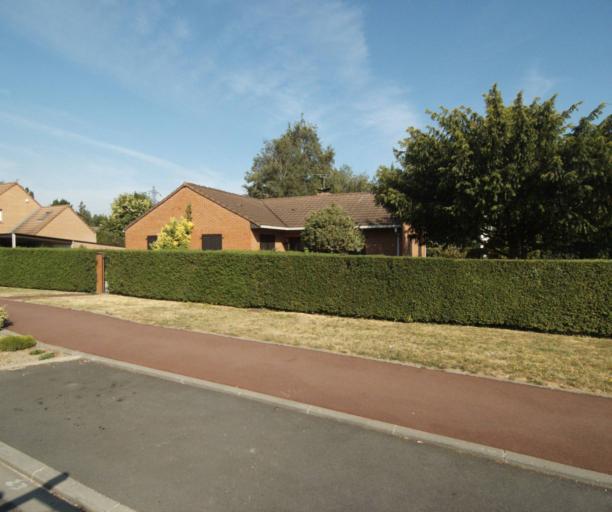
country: FR
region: Nord-Pas-de-Calais
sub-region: Departement du Nord
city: Mouvaux
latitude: 50.7094
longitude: 3.1341
